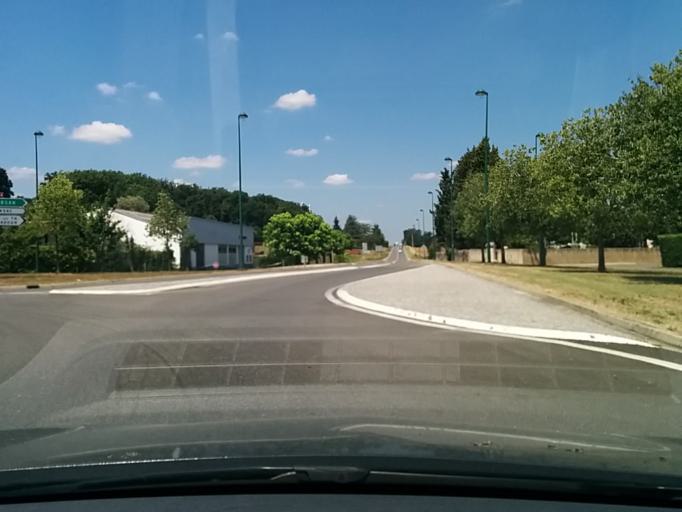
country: FR
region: Midi-Pyrenees
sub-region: Departement du Gers
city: Vic-Fezensac
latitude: 43.7262
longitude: 0.3758
